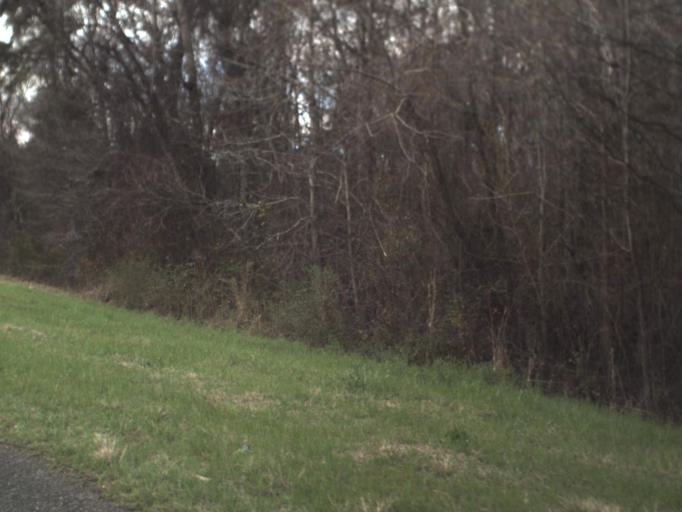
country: US
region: Florida
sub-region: Jackson County
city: Marianna
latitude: 30.8243
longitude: -85.3625
